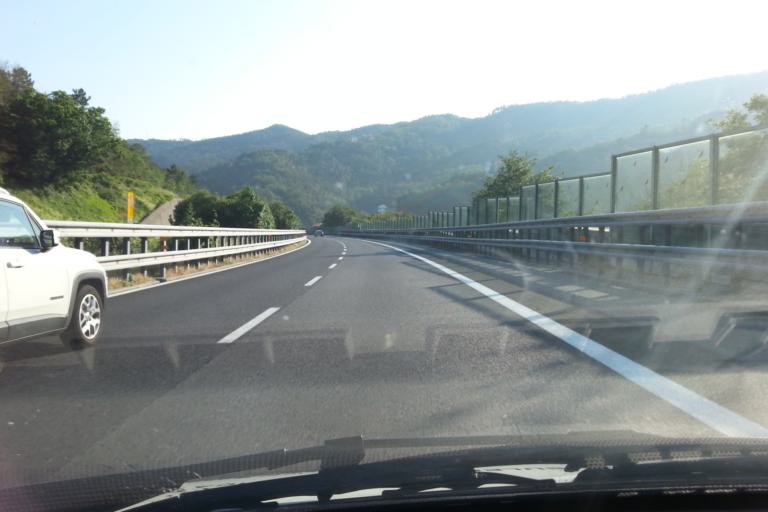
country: IT
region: Liguria
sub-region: Provincia di Savona
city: Orco Feglino
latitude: 44.2219
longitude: 8.3287
